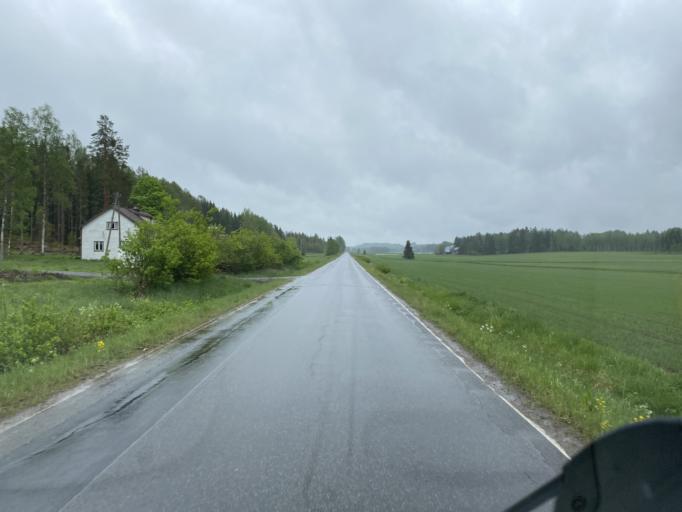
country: FI
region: Haeme
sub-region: Forssa
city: Humppila
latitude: 61.0470
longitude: 23.3716
